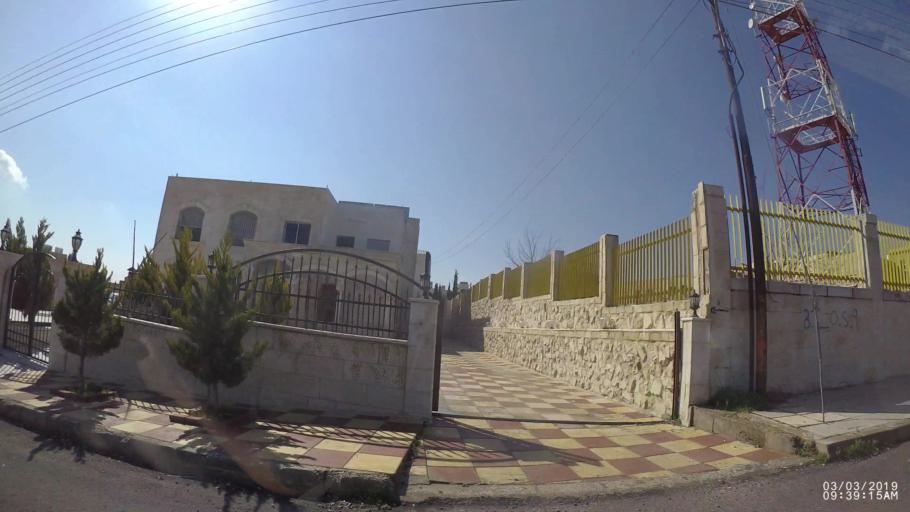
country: JO
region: Amman
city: Al Jubayhah
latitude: 31.9995
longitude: 35.8966
